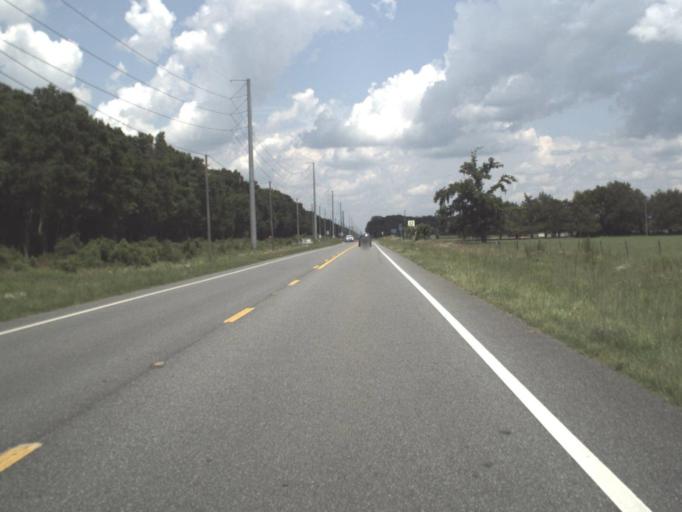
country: US
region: Florida
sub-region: Gilchrist County
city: Trenton
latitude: 29.6121
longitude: -82.9099
